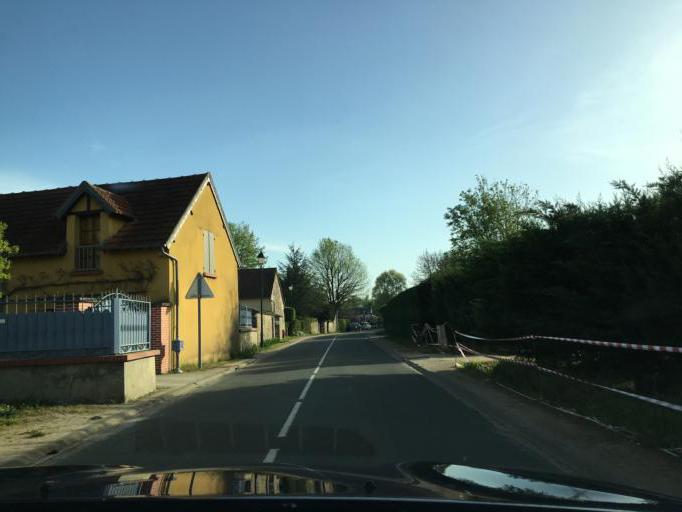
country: FR
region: Centre
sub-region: Departement d'Eure-et-Loir
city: Epernon
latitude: 48.6173
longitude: 1.6734
